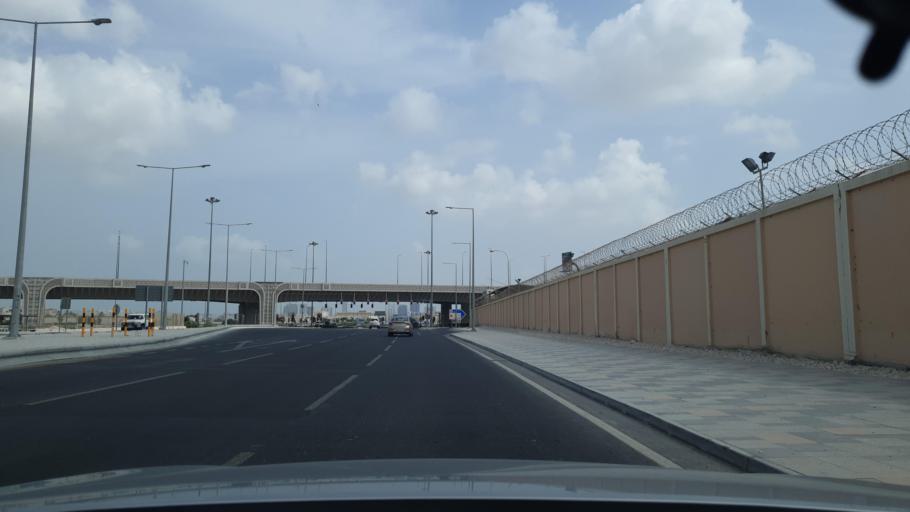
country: QA
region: Baladiyat ar Rayyan
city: Ar Rayyan
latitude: 25.2785
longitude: 51.4702
